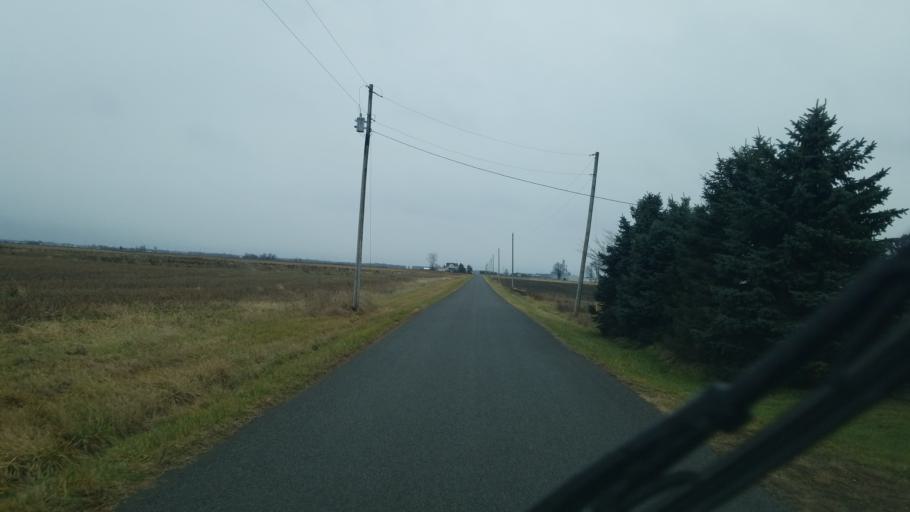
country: US
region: Ohio
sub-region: Logan County
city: Northwood
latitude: 40.4491
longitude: -83.5657
